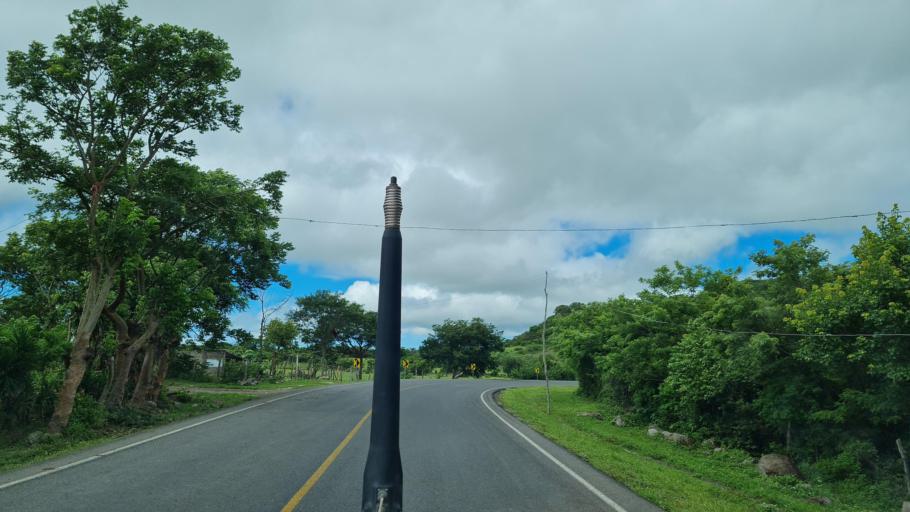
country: NI
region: Matagalpa
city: Terrabona
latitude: 12.5841
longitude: -85.9732
